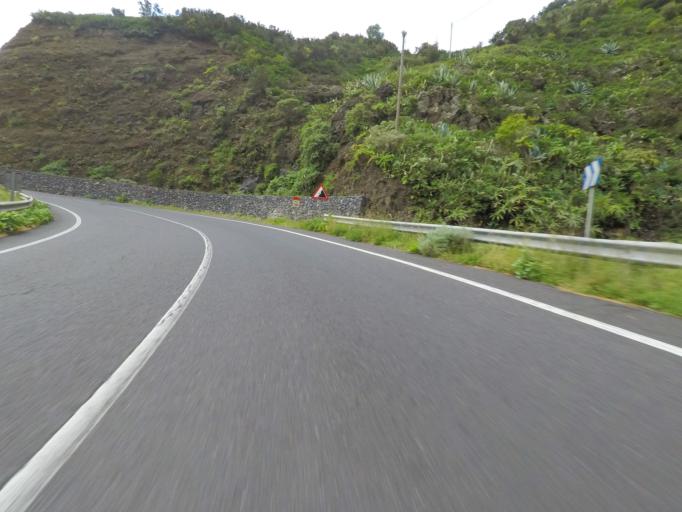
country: ES
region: Canary Islands
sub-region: Provincia de Santa Cruz de Tenerife
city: Hermigua
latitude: 28.1321
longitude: -17.1830
